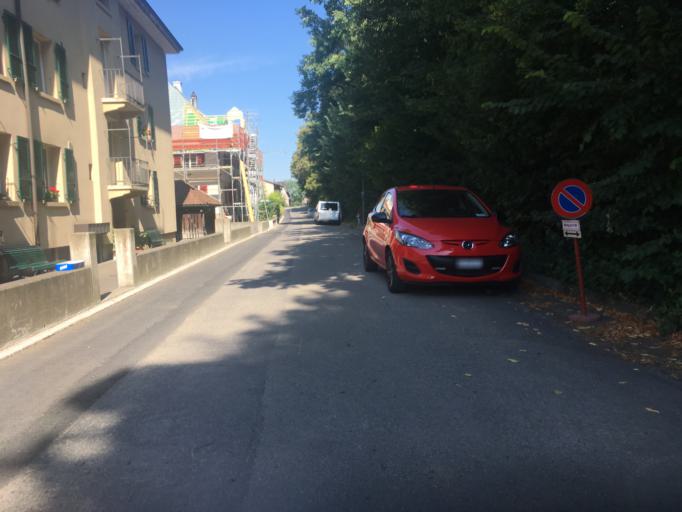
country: CH
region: Bern
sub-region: Emmental District
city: Burgdorf
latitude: 47.0639
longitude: 7.6212
